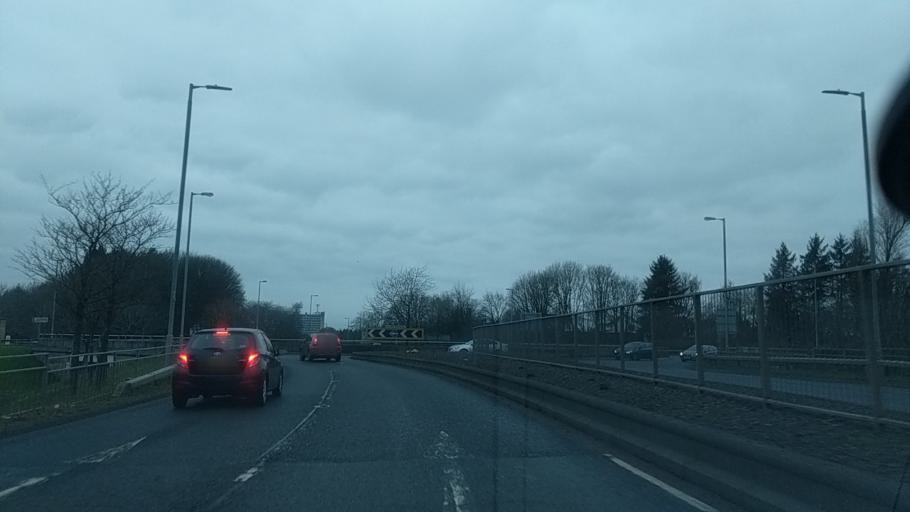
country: GB
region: Scotland
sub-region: South Lanarkshire
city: East Kilbride
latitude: 55.7575
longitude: -4.1647
